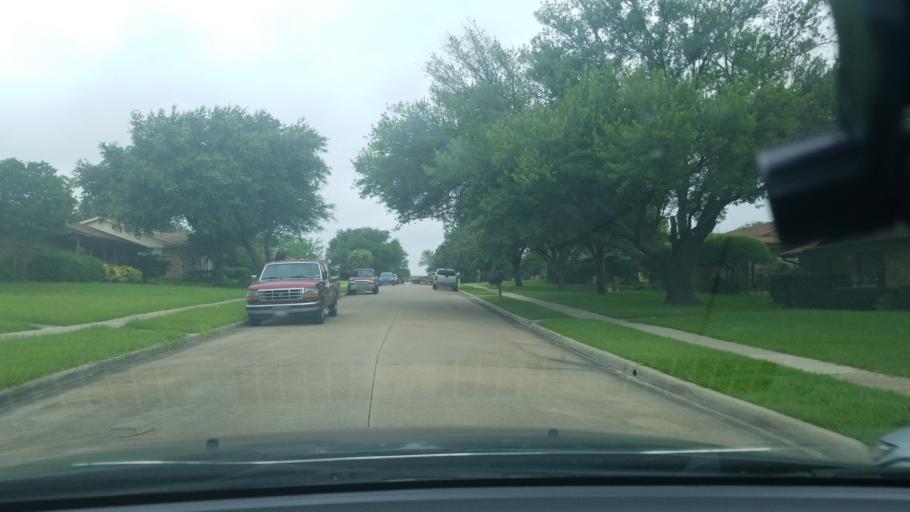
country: US
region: Texas
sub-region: Dallas County
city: Mesquite
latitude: 32.7823
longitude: -96.6408
